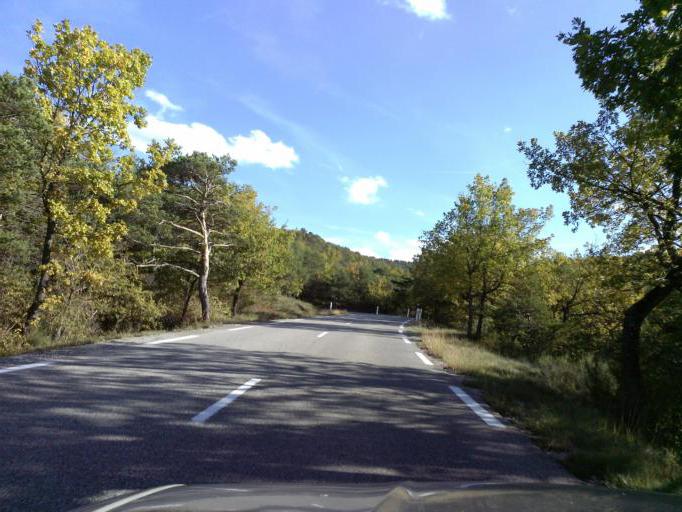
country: FR
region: Provence-Alpes-Cote d'Azur
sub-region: Departement des Alpes-de-Haute-Provence
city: Riez
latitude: 43.9117
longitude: 6.1383
